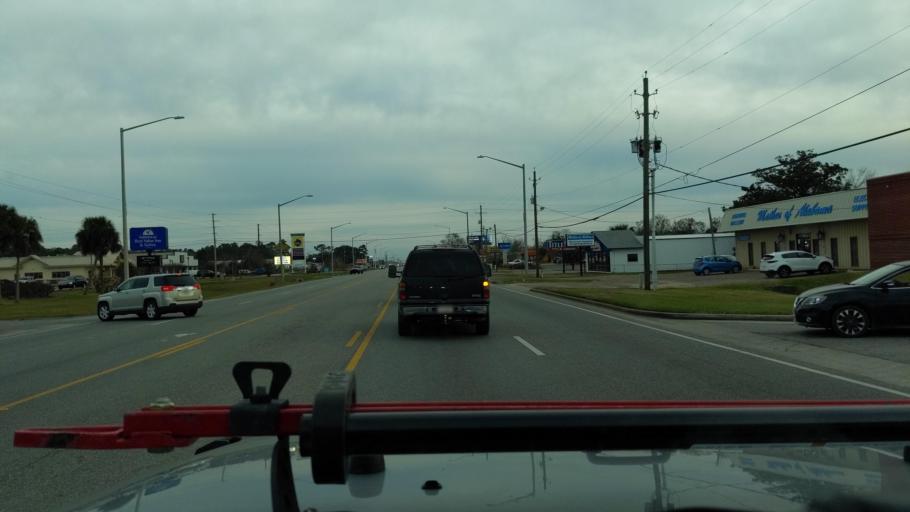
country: US
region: Alabama
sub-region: Baldwin County
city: Foley
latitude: 30.3897
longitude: -87.6834
